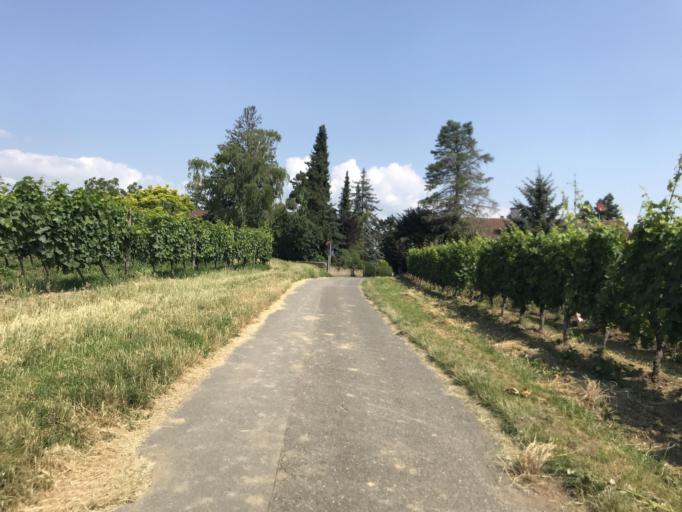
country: DE
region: Hesse
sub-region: Regierungsbezirk Darmstadt
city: Hochheim am Main
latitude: 50.0083
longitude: 8.3597
